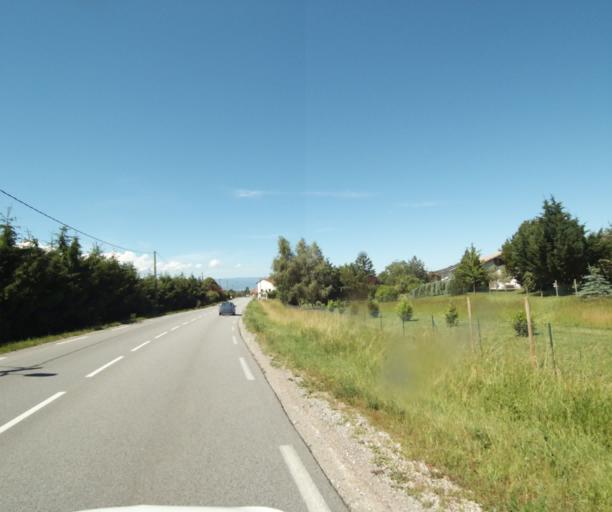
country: FR
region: Rhone-Alpes
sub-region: Departement de la Haute-Savoie
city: Loisin
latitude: 46.2827
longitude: 6.3095
